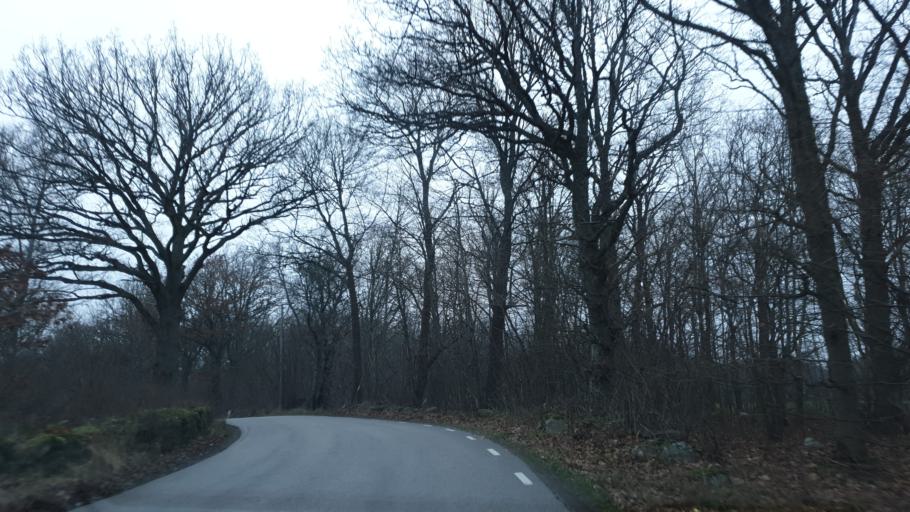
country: SE
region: Blekinge
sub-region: Karlskrona Kommun
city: Rodeby
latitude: 56.2024
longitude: 15.6856
